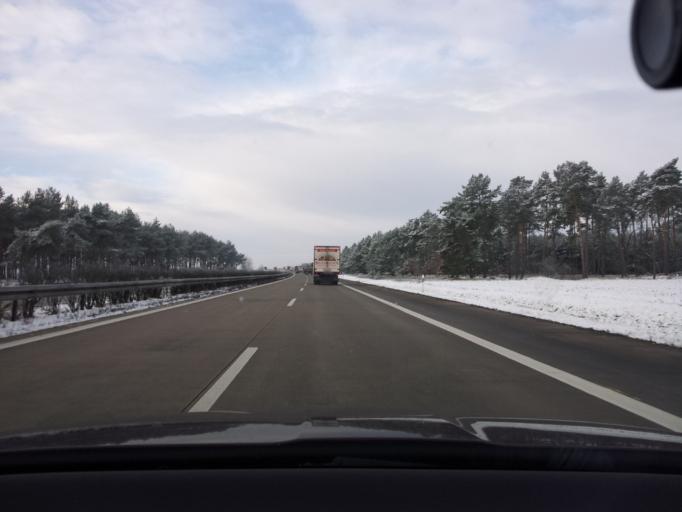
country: DE
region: Mecklenburg-Vorpommern
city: Rastow
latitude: 53.4318
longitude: 11.4649
